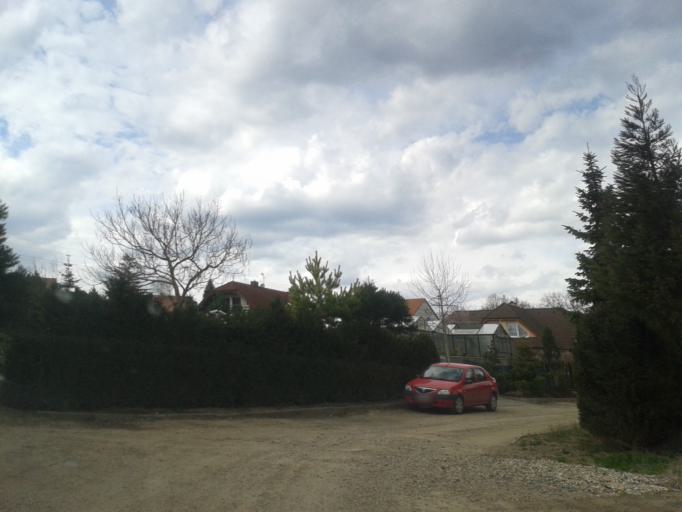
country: CZ
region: Central Bohemia
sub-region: Okres Beroun
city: Lodenice
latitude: 50.0064
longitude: 14.1555
